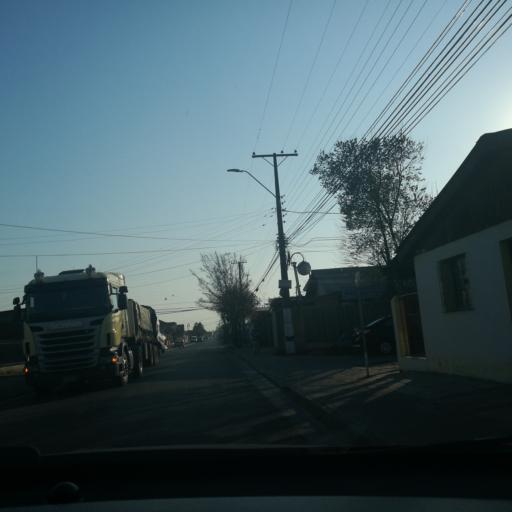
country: CL
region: O'Higgins
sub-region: Provincia de Cachapoal
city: Rancagua
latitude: -34.1715
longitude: -70.7123
